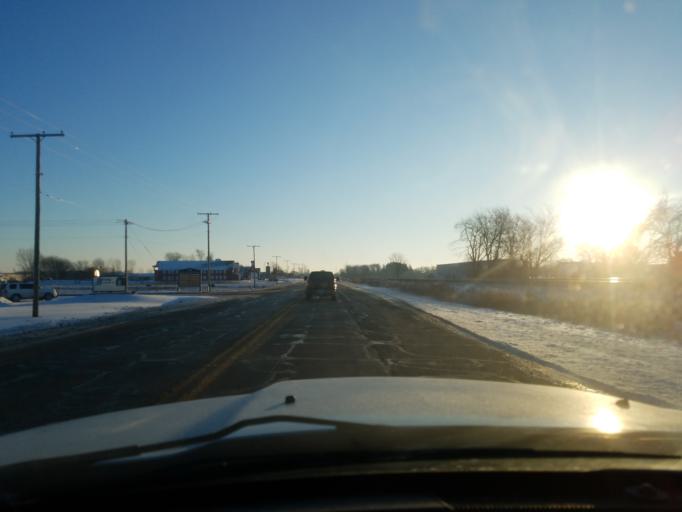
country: US
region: Indiana
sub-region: Elkhart County
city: Nappanee
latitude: 41.4437
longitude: -86.0351
